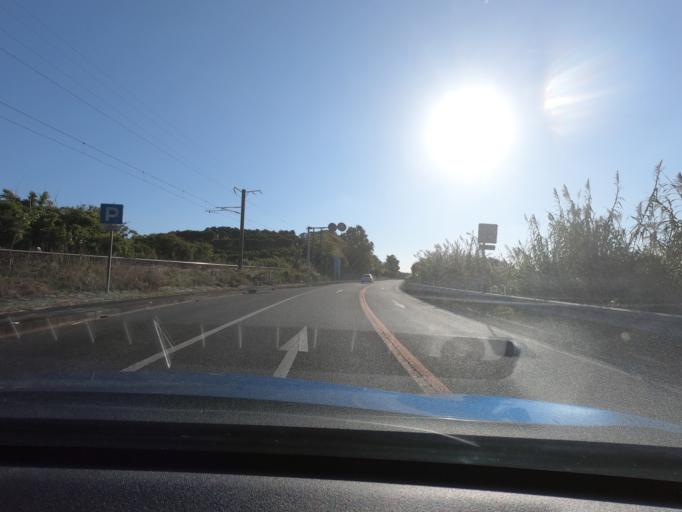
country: JP
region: Kagoshima
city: Izumi
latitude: 32.1357
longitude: 130.3525
